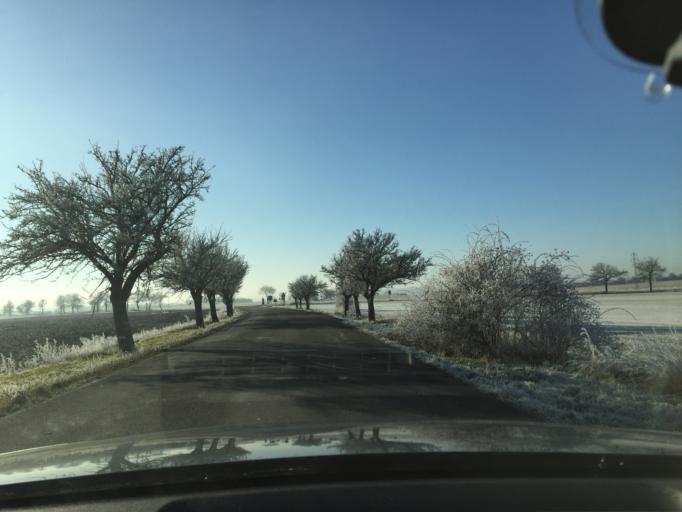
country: CZ
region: Central Bohemia
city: Trebotov
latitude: 50.0128
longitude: 14.2887
